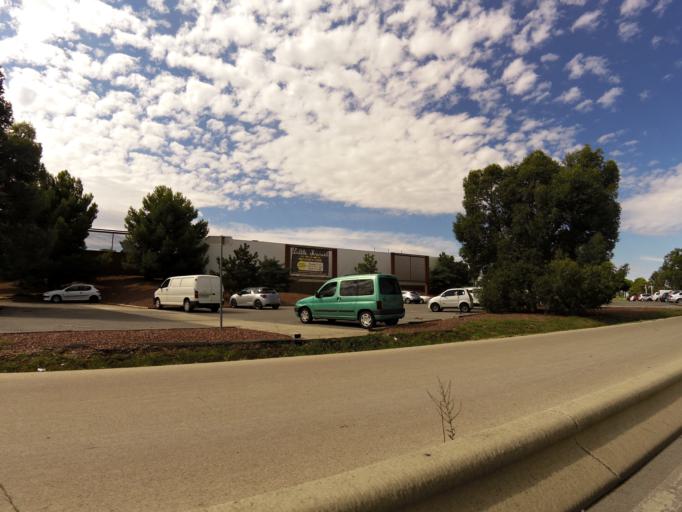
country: FR
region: Languedoc-Roussillon
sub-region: Departement du Gard
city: Le Grau-du-Roi
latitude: 43.5243
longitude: 4.1497
